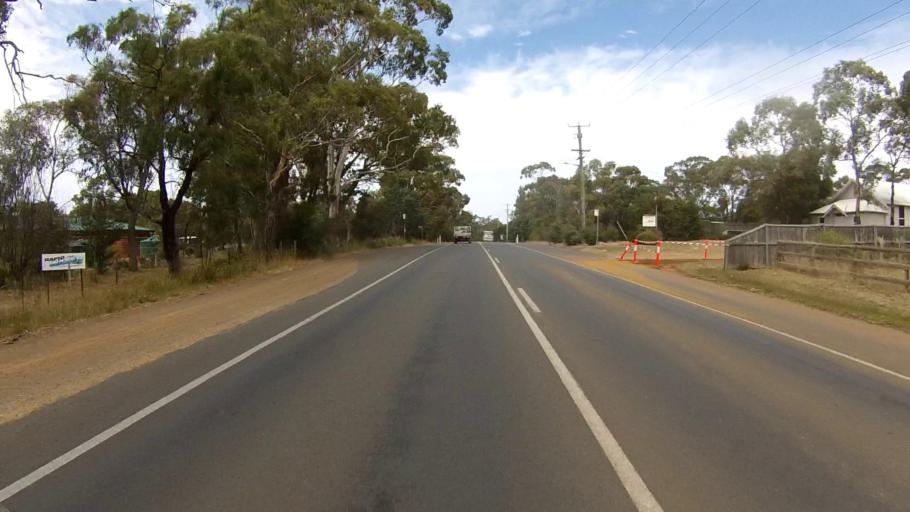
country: AU
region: Tasmania
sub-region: Clarence
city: Sandford
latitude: -42.9392
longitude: 147.4957
